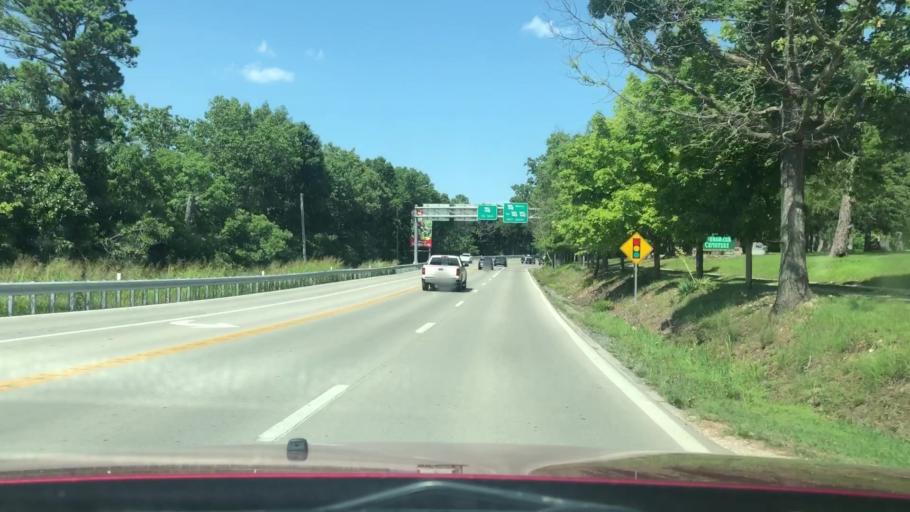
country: US
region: Missouri
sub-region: Stone County
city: Kimberling City
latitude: 36.6734
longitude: -93.3296
